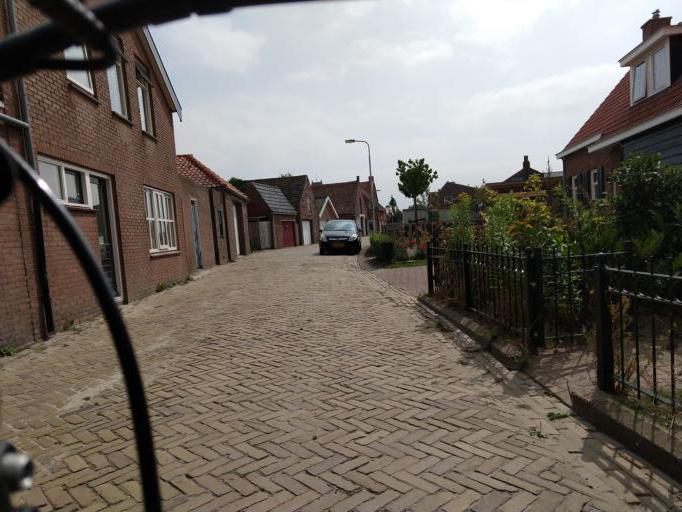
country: NL
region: Zeeland
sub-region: Schouwen-Duiveland
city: Bruinisse
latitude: 51.6493
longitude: 4.0335
